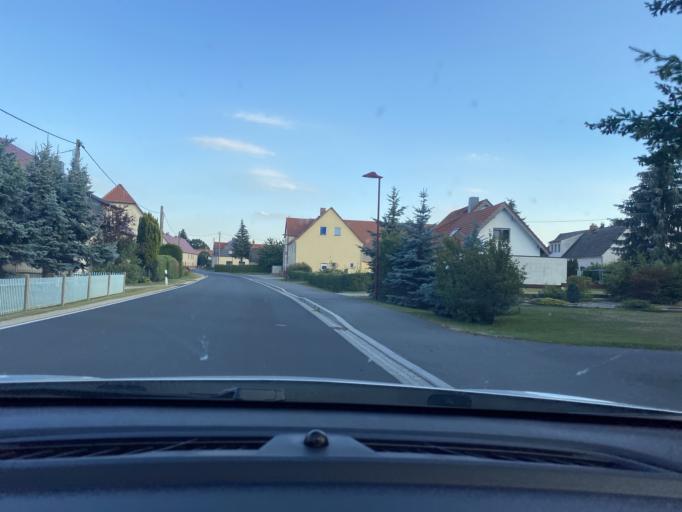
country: DE
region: Saxony
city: Kodersdorf
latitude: 51.2589
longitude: 14.8872
